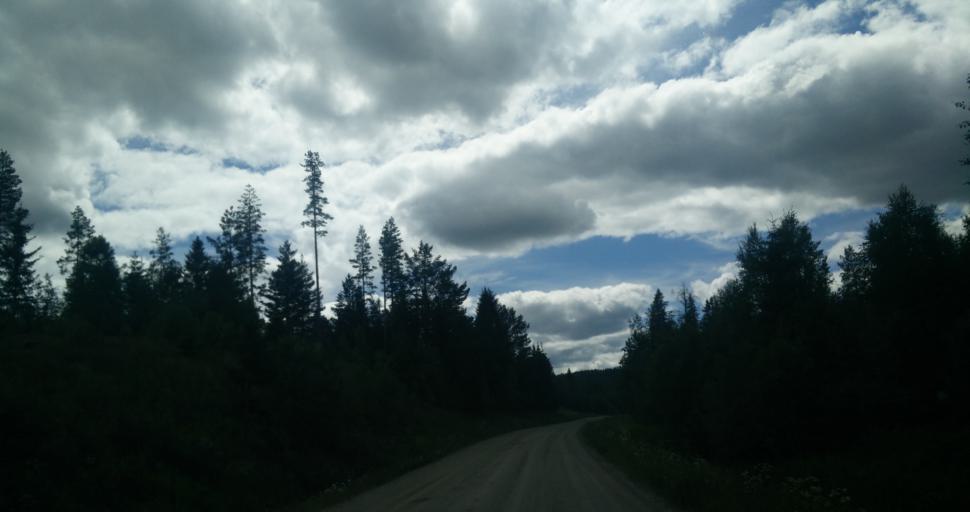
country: SE
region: Gaevleborg
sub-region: Nordanstigs Kommun
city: Bergsjoe
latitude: 62.1195
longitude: 17.1009
